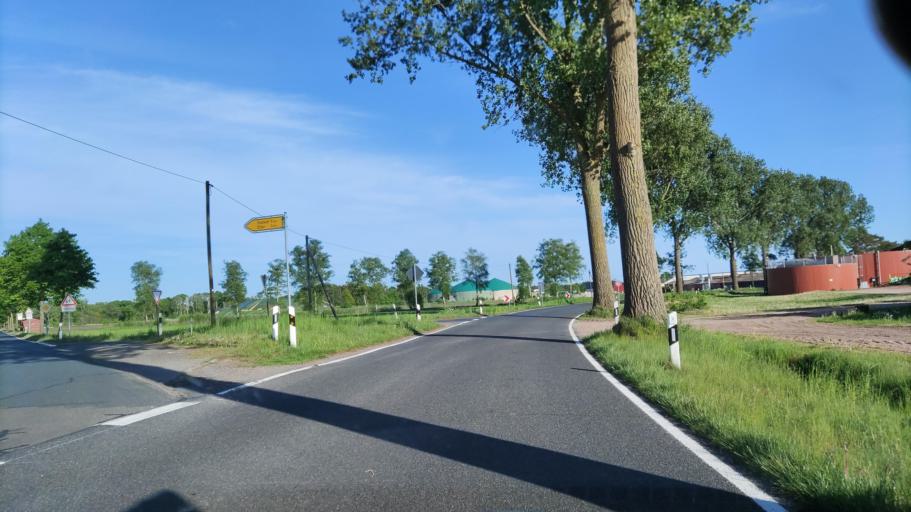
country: DE
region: Lower Saxony
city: Otter
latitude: 53.2197
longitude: 9.7147
